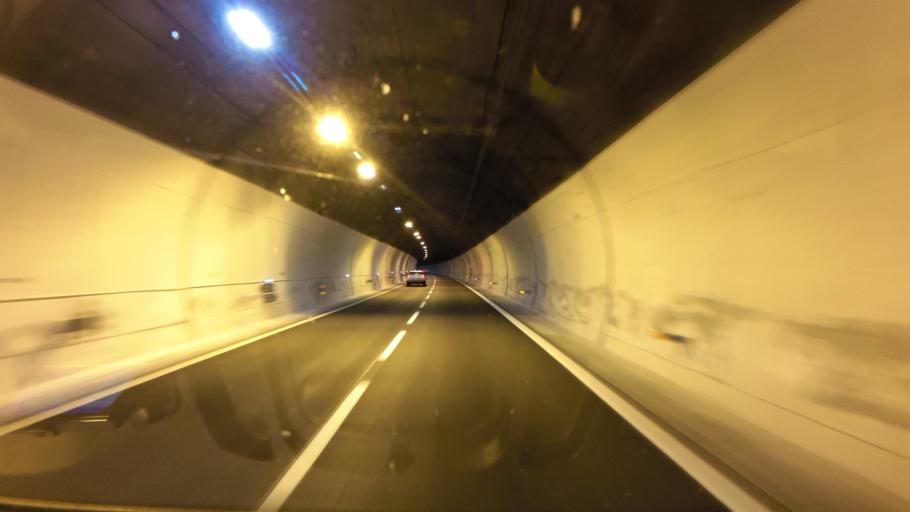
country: IT
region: Friuli Venezia Giulia
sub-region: Provincia di Udine
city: Dogna
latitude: 46.4609
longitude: 13.3041
